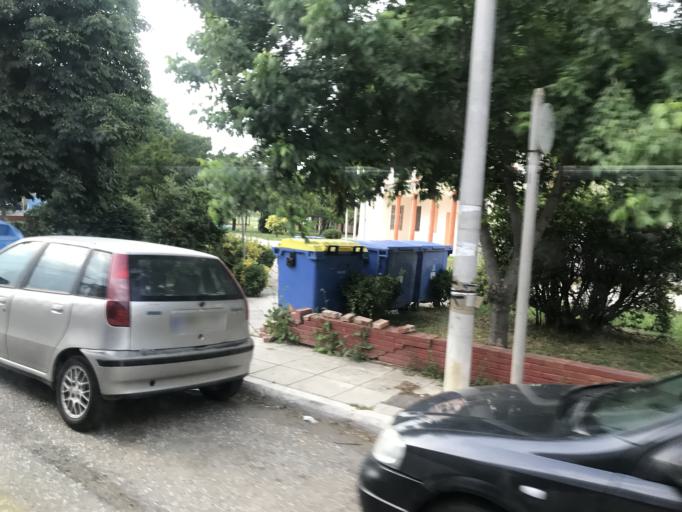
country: GR
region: East Macedonia and Thrace
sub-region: Nomos Rodopis
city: Sapes
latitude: 41.0236
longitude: 25.6926
